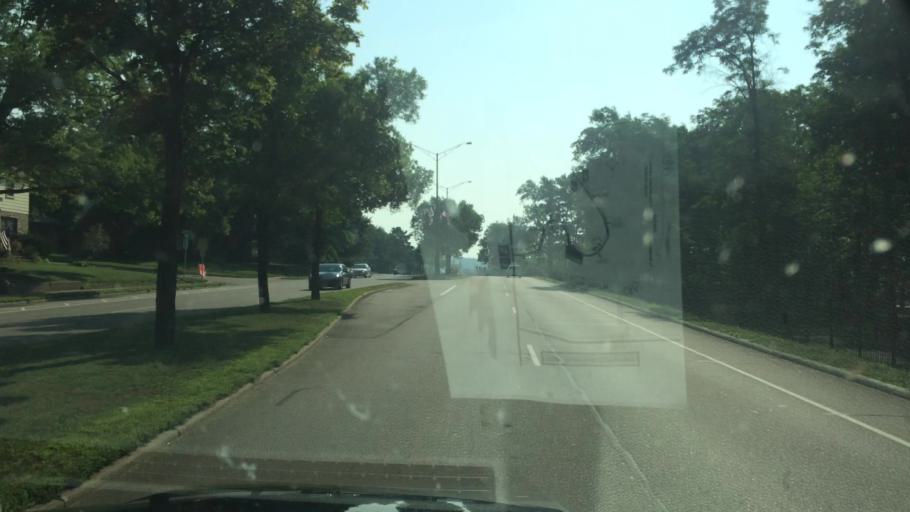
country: US
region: Wisconsin
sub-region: Marathon County
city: Wausau
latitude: 44.9591
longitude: -89.6474
